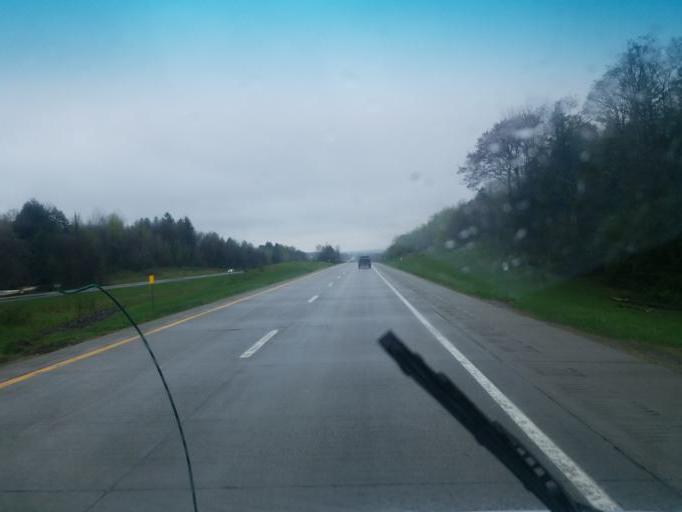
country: US
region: New York
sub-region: Chautauqua County
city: Mayville
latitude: 42.1569
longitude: -79.5410
